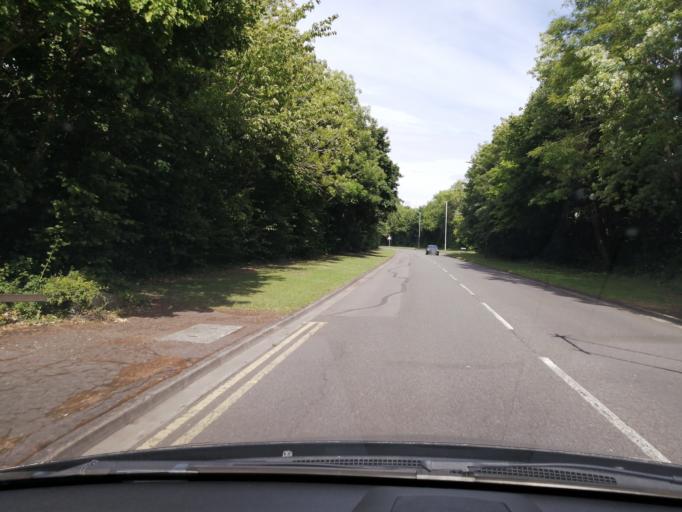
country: GB
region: England
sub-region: Peterborough
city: Castor
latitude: 52.5499
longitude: -0.3051
